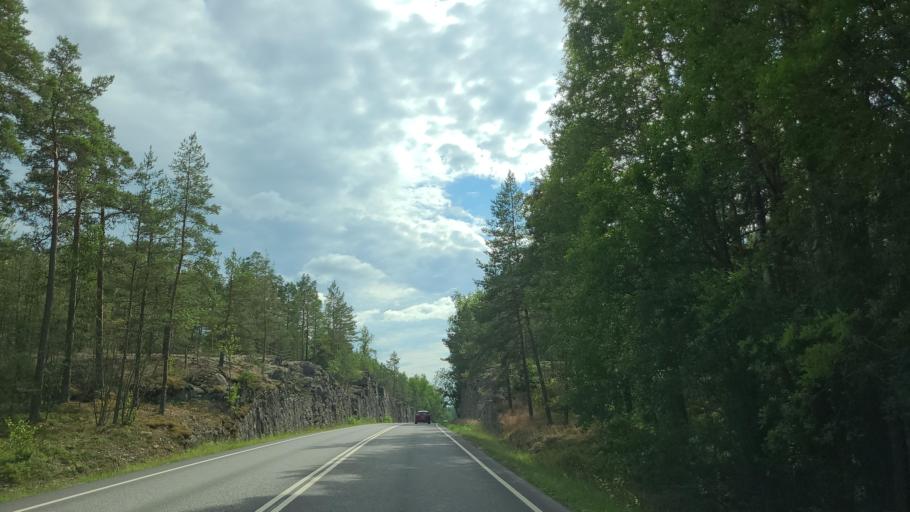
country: FI
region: Varsinais-Suomi
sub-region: Turku
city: Merimasku
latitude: 60.4558
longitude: 21.9091
